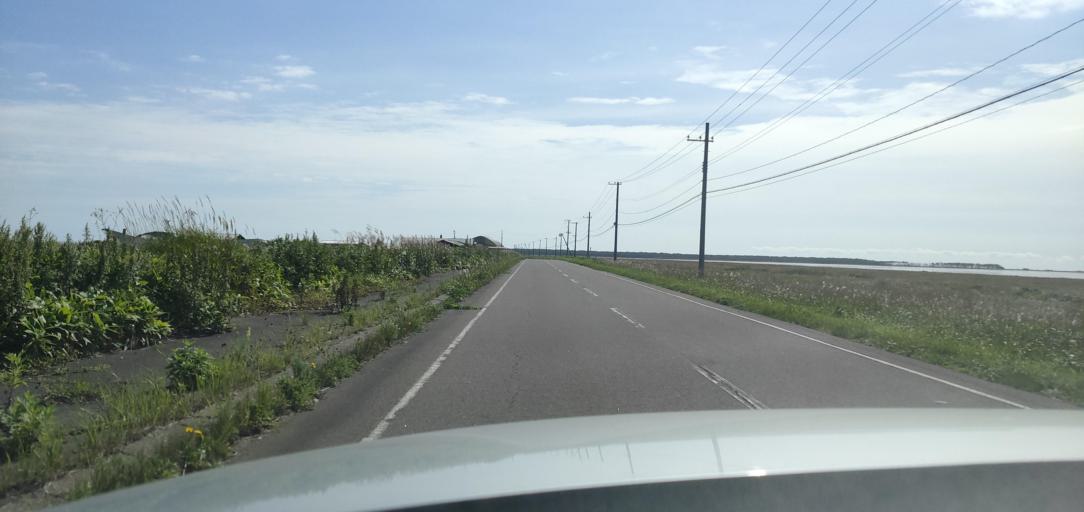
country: JP
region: Hokkaido
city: Shibetsu
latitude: 43.6171
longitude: 145.2369
